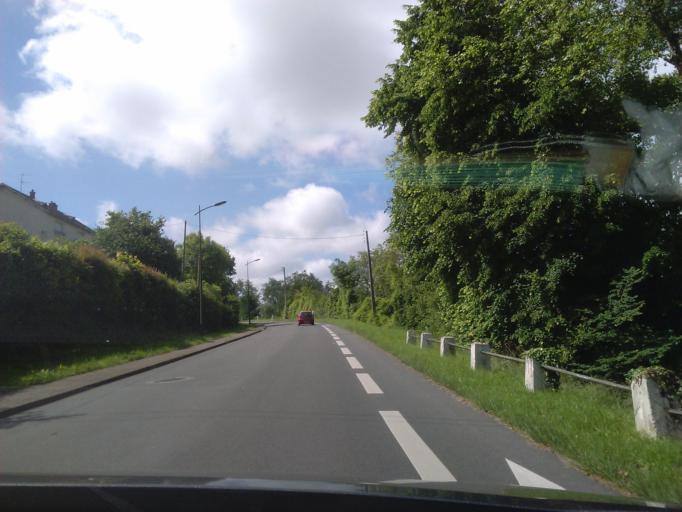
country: FR
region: Centre
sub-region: Departement du Loir-et-Cher
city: Vendome
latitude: 47.7855
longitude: 1.0637
